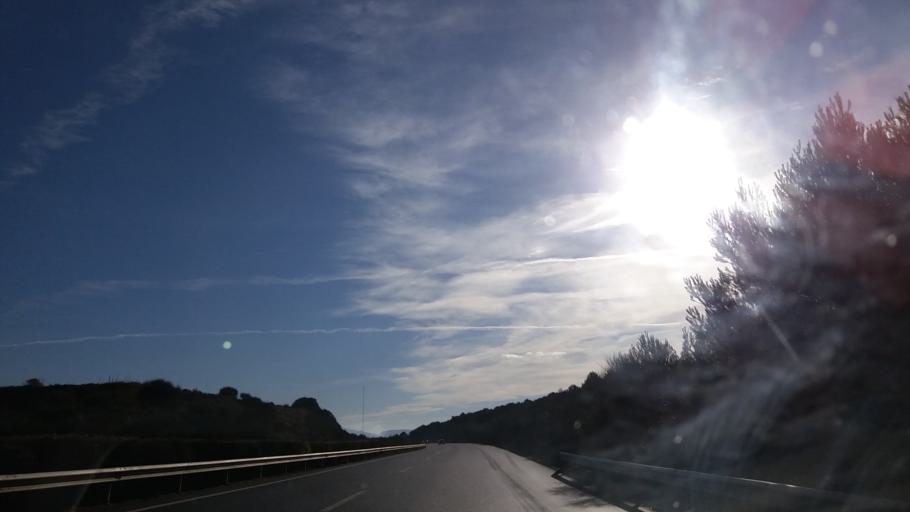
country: ES
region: Navarre
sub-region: Provincia de Navarra
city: Berriobeiti
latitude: 42.8518
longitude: -1.7106
